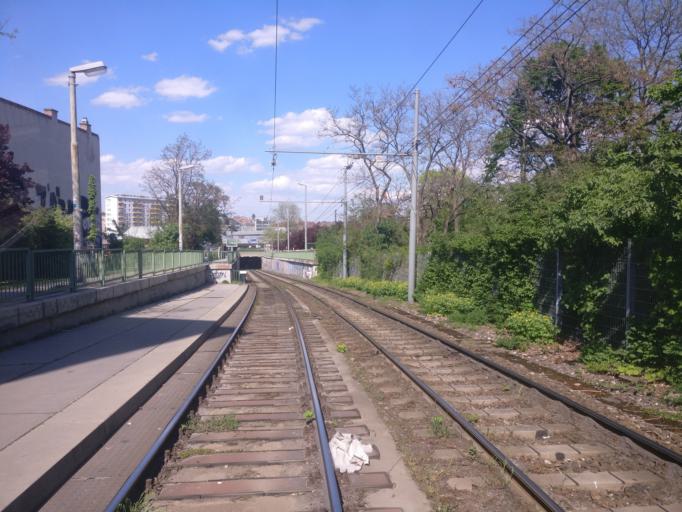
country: AT
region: Vienna
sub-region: Wien Stadt
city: Vienna
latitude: 48.1780
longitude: 16.3585
